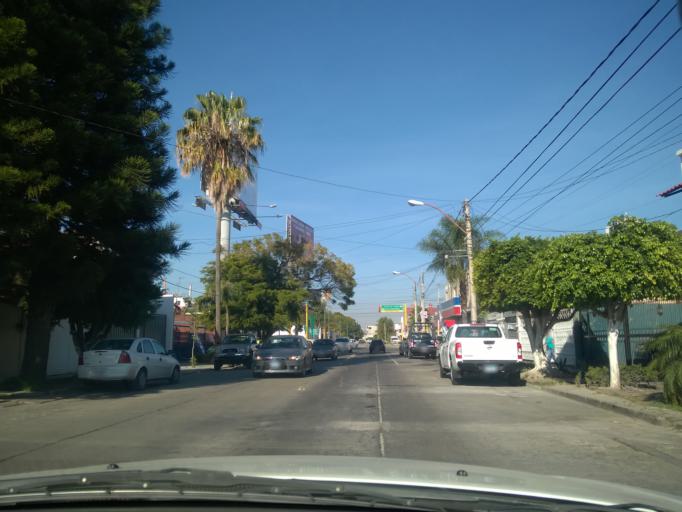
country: MX
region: Guanajuato
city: Leon
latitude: 21.1168
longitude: -101.6514
